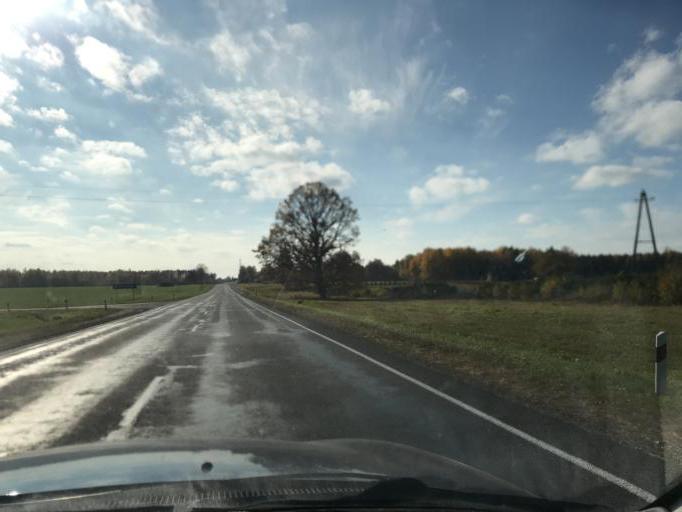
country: BY
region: Grodnenskaya
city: Voranava
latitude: 54.1815
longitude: 25.3354
